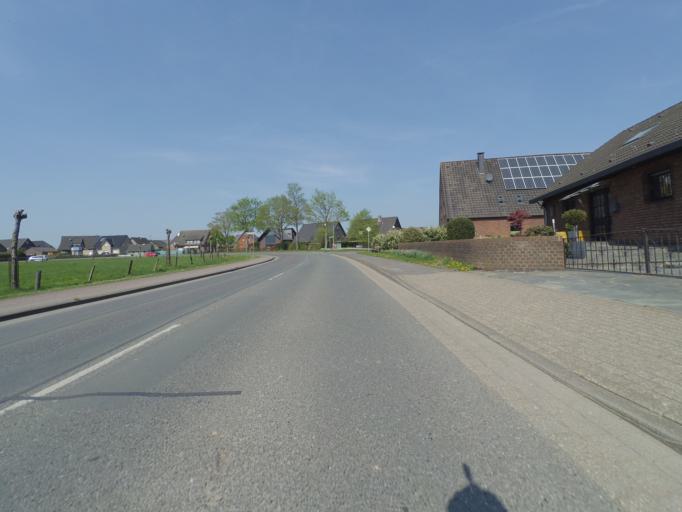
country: DE
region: North Rhine-Westphalia
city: Rees
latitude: 51.8101
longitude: 6.3934
